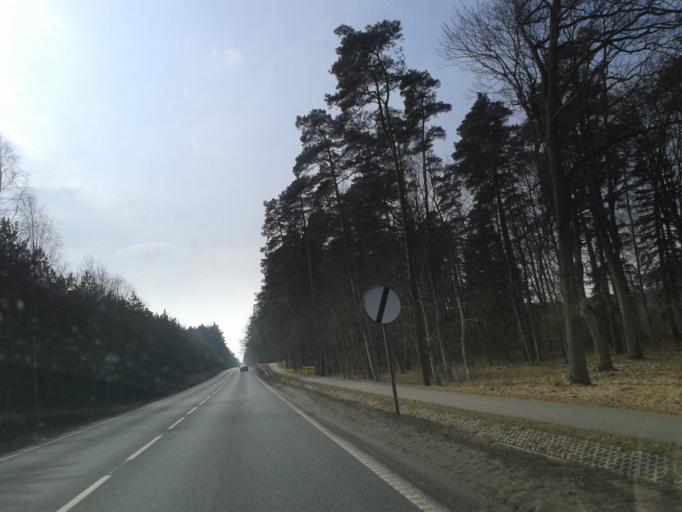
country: PL
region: Pomeranian Voivodeship
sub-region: Powiat czluchowski
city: Czluchow
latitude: 53.6496
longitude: 17.3153
